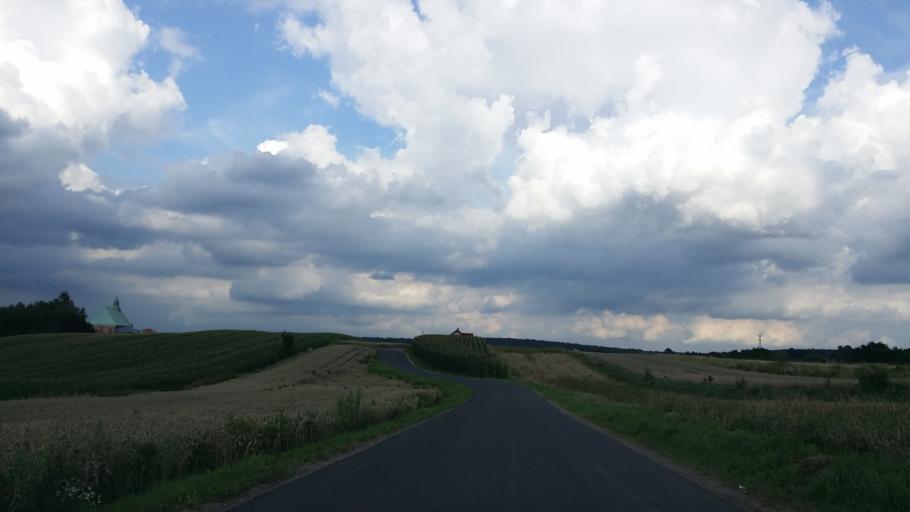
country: PL
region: Lesser Poland Voivodeship
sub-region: Powiat wadowicki
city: Bachowice
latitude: 49.9649
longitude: 19.4851
